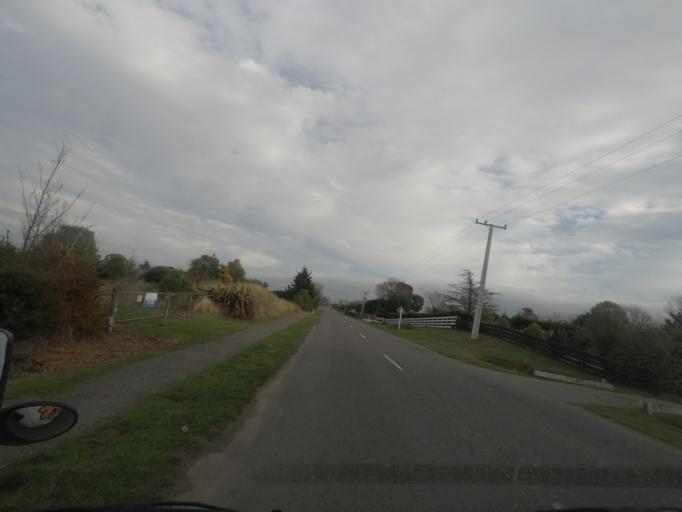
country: NZ
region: Canterbury
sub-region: Waimakariri District
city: Woodend
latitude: -43.2874
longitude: 172.7094
